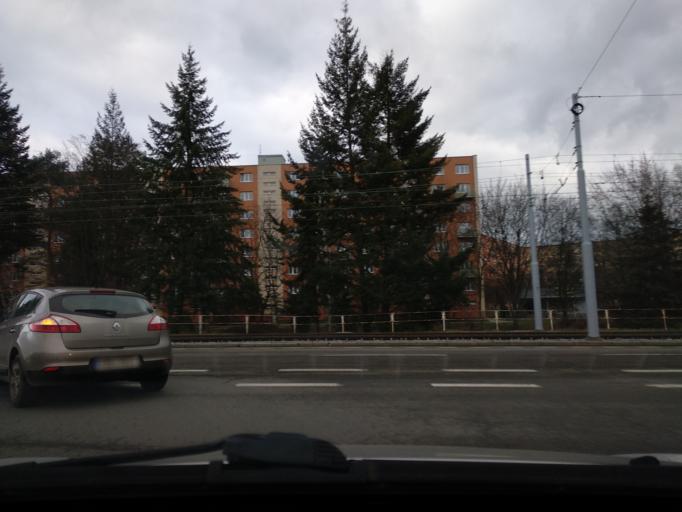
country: CZ
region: South Moravian
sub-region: Mesto Brno
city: Brno
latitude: 49.2191
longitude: 16.6179
